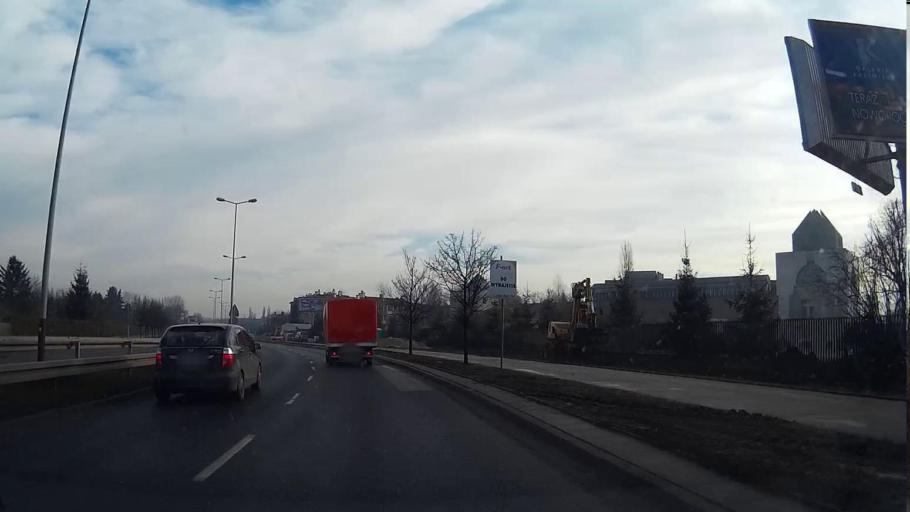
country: PL
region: Lesser Poland Voivodeship
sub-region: Krakow
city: Krakow
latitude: 50.0444
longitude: 19.9161
